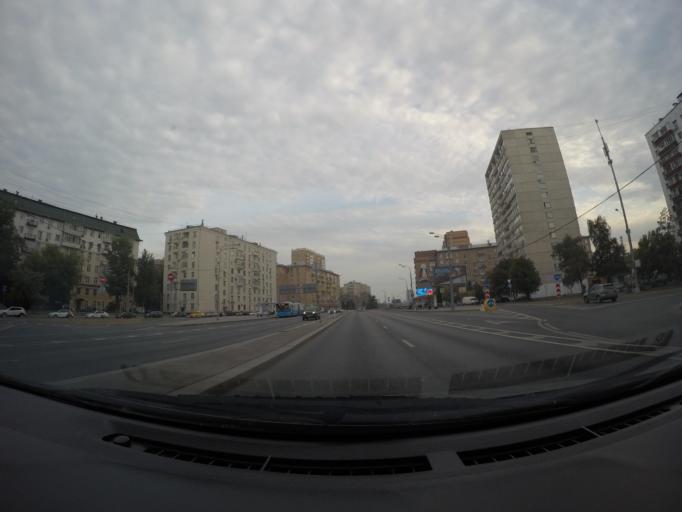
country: RU
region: Moskovskaya
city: Kozhukhovo
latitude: 55.7067
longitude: 37.6673
